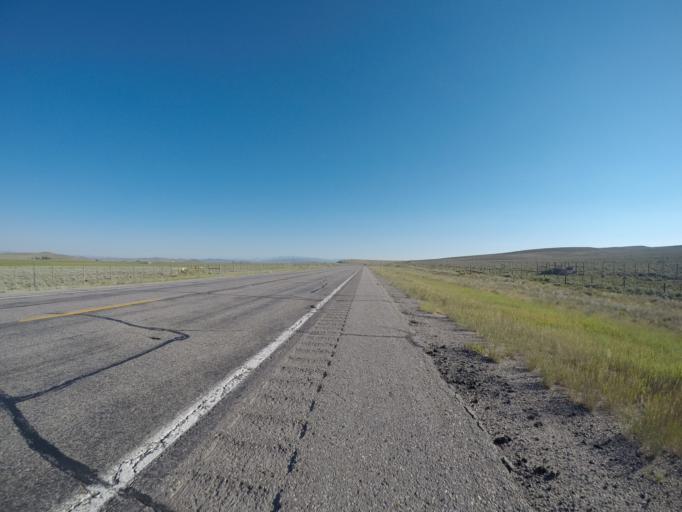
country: US
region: Wyoming
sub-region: Sublette County
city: Pinedale
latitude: 42.9289
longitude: -110.0810
